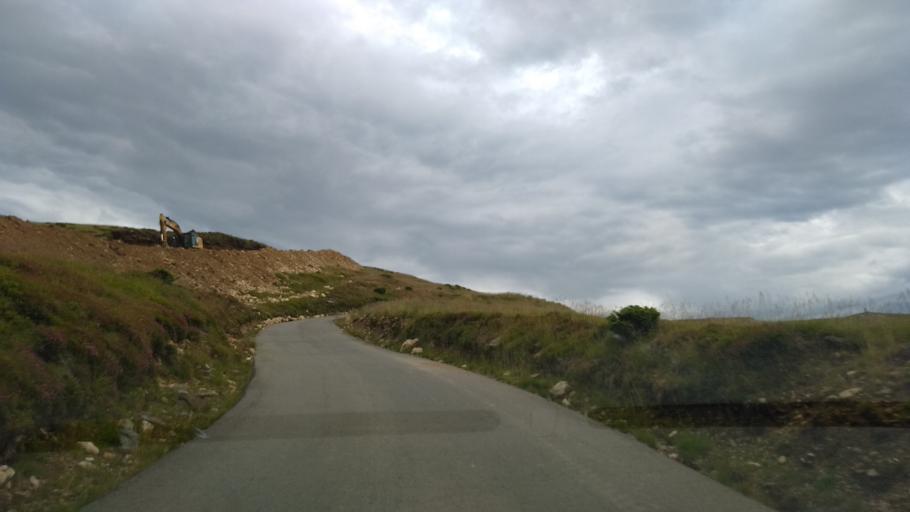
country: RO
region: Hunedoara
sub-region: Municipiul  Vulcan
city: Jiu-Paroseni
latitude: 45.3068
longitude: 23.3119
